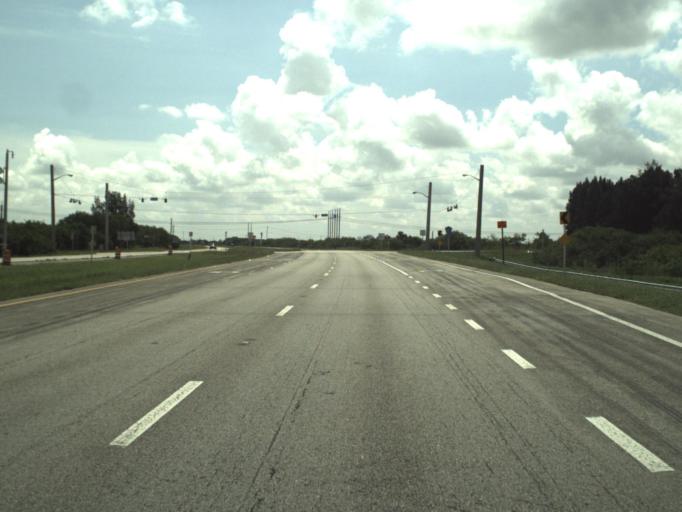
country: US
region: Florida
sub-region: Palm Beach County
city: Loxahatchee Groves
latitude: 26.6877
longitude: -80.3891
